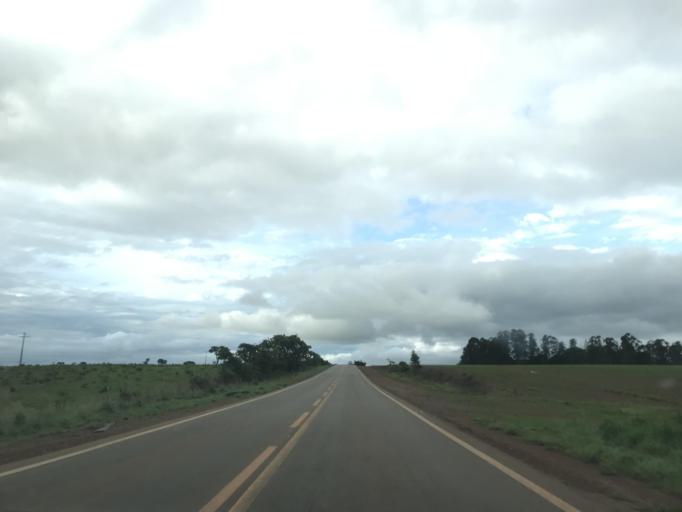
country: BR
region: Goias
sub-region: Luziania
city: Luziania
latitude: -16.4561
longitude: -48.2083
